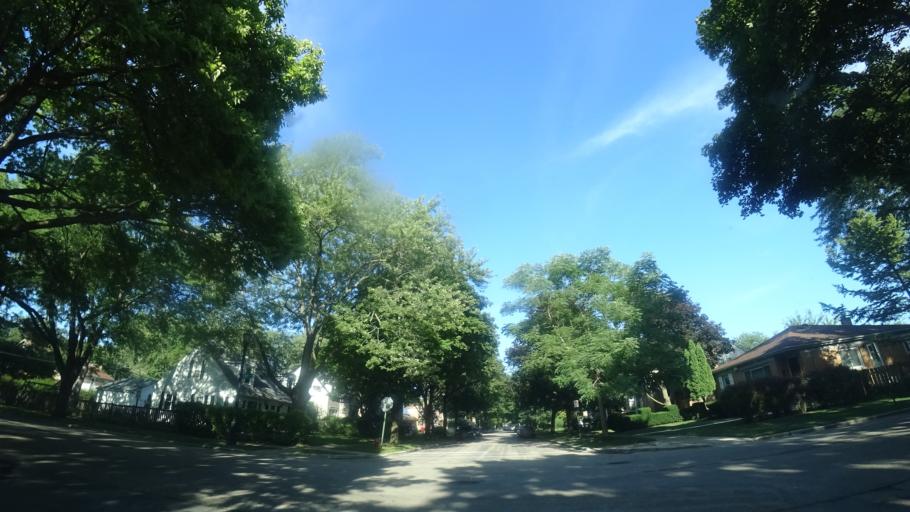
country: US
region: Illinois
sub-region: Cook County
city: Evanston
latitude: 42.0293
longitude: -87.7018
